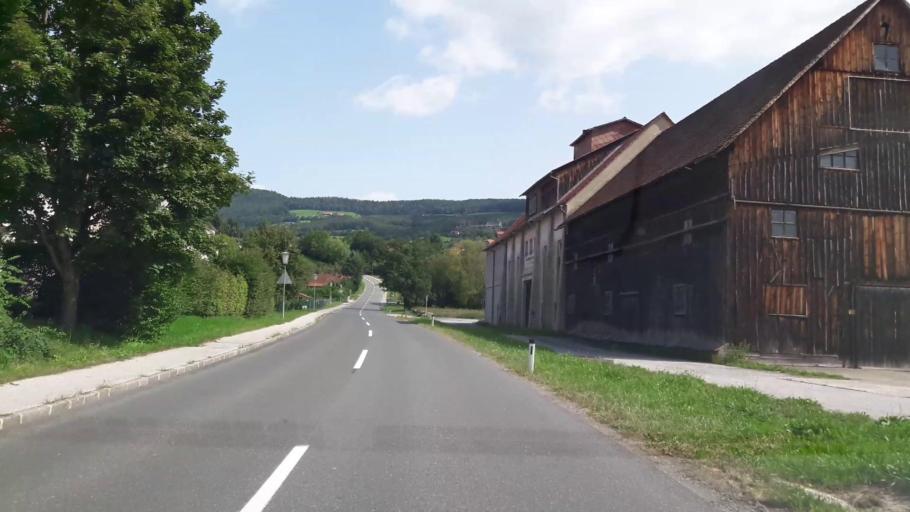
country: AT
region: Styria
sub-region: Politischer Bezirk Hartberg-Fuerstenfeld
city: Stubenberg
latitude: 47.2407
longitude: 15.7951
